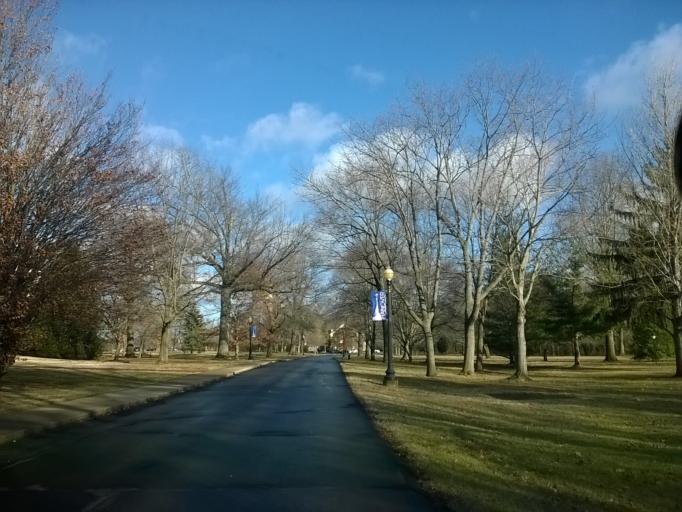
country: US
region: Indiana
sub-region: Jefferson County
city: Hanover
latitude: 38.7162
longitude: -85.4610
